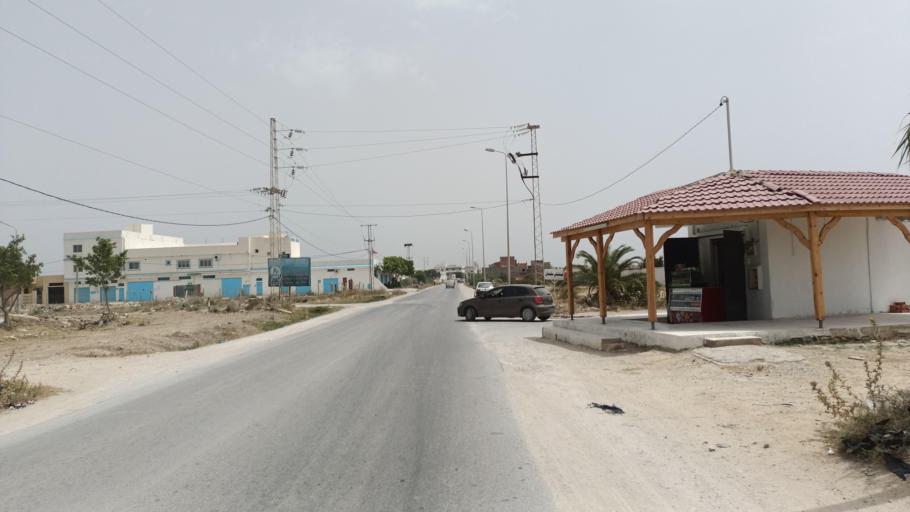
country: TN
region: Nabul
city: Manzil Bu Zalafah
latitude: 36.7108
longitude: 10.4823
